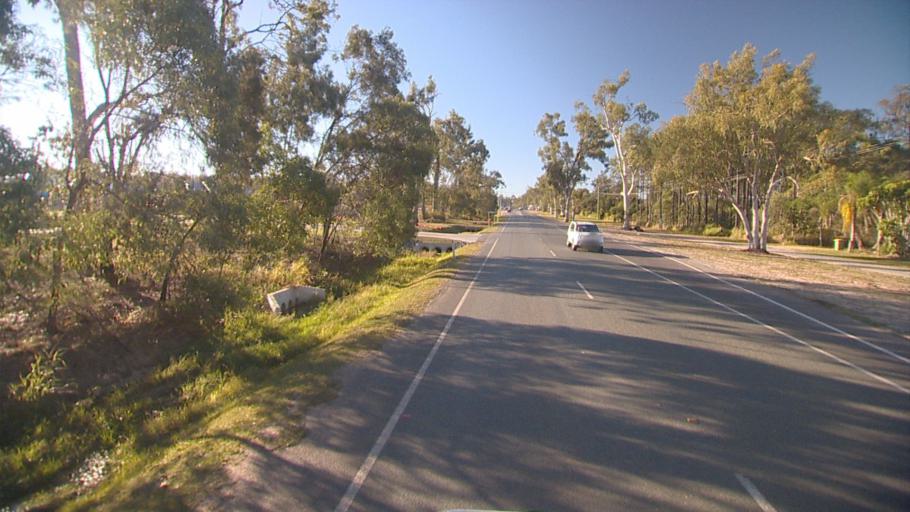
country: AU
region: Queensland
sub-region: Logan
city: Logan Reserve
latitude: -27.7137
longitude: 153.0929
